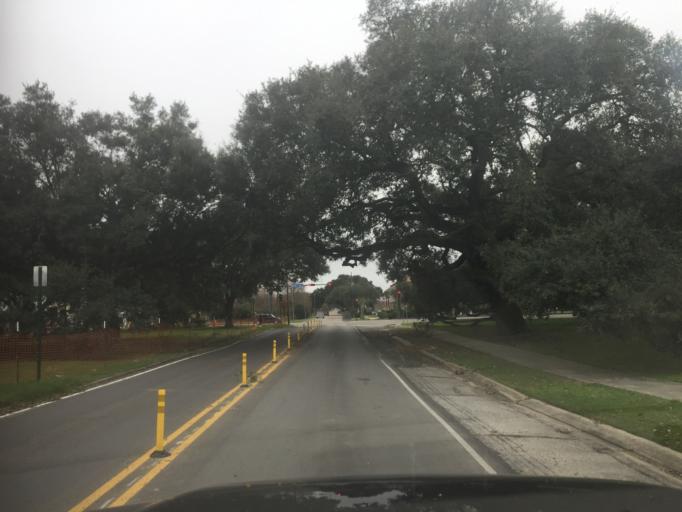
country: US
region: Louisiana
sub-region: Jefferson Parish
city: Metairie
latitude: 30.0204
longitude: -90.1064
